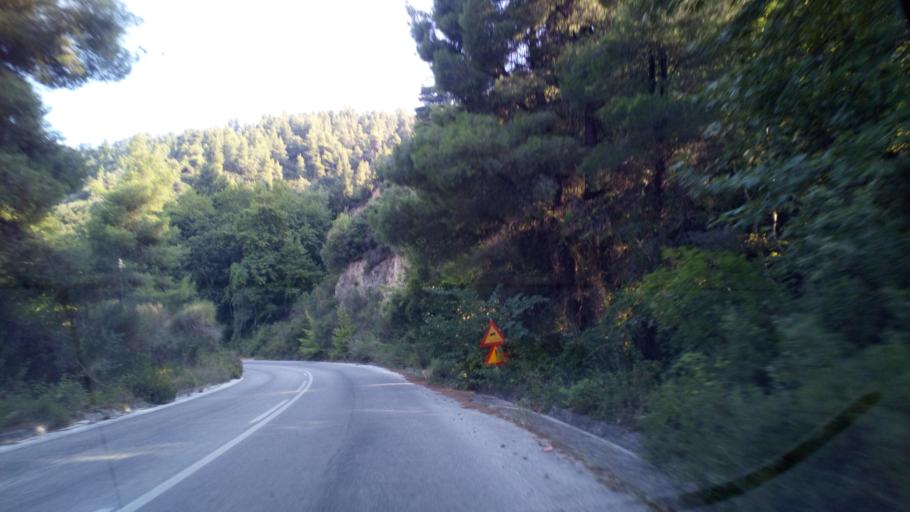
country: GR
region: Central Macedonia
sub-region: Nomos Chalkidikis
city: Neos Marmaras
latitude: 40.1718
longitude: 23.8503
